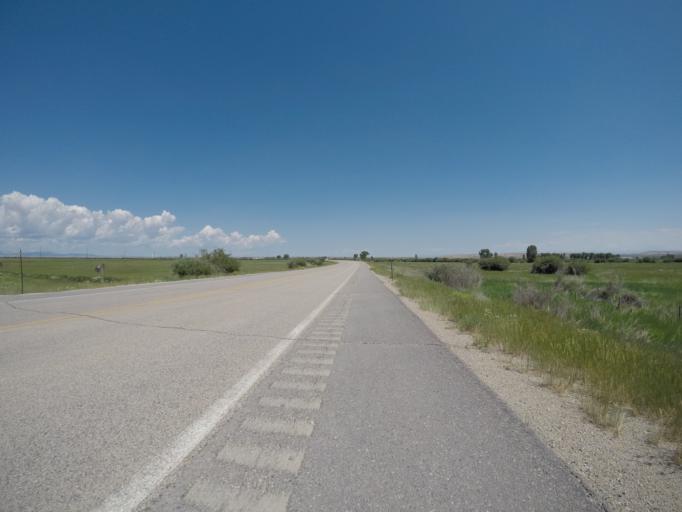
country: US
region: Wyoming
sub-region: Sublette County
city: Marbleton
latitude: 42.5154
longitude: -110.1050
